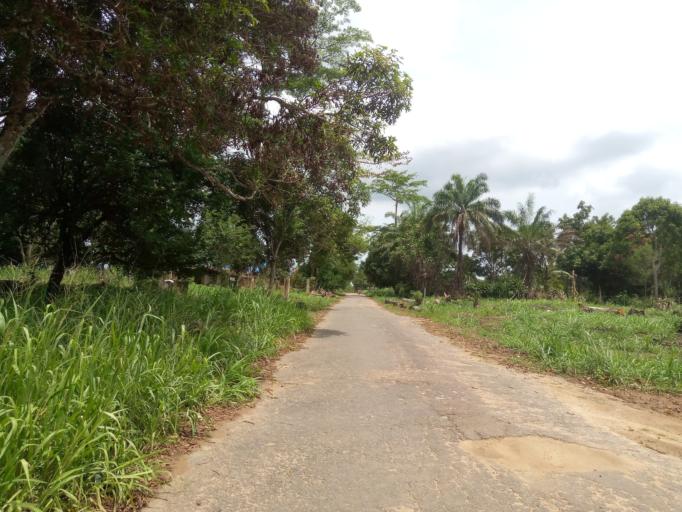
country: SL
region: Western Area
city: Waterloo
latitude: 8.3440
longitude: -12.9851
